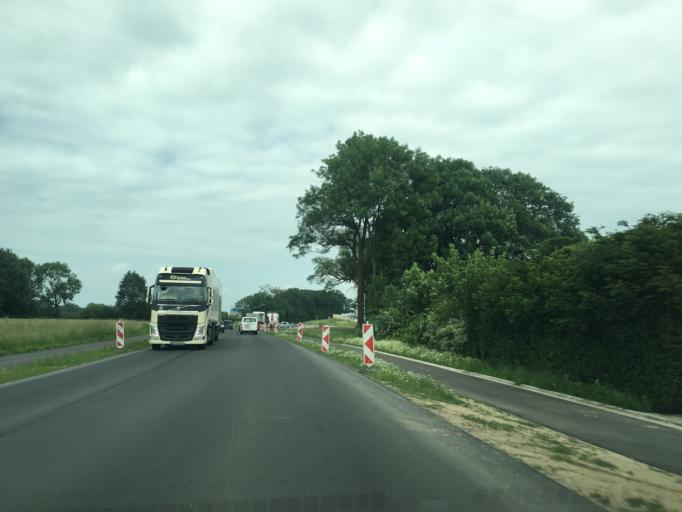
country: DE
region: North Rhine-Westphalia
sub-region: Regierungsbezirk Munster
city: Altenberge
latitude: 52.0747
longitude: 7.4447
